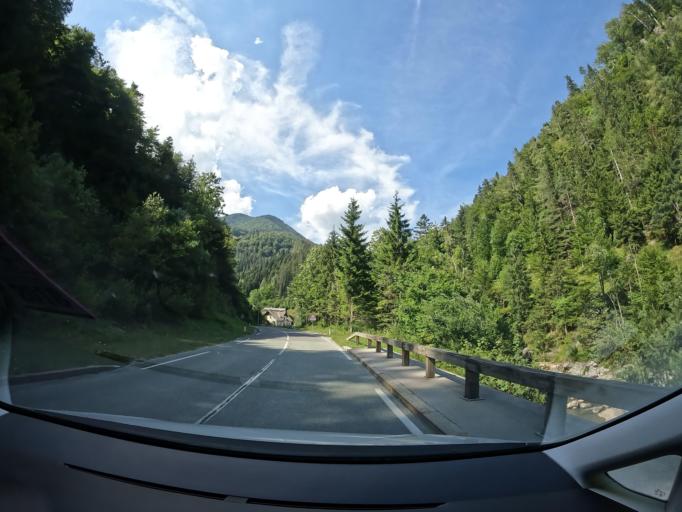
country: SI
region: Zirovnica
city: Zirovnica
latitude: 46.4337
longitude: 14.2215
